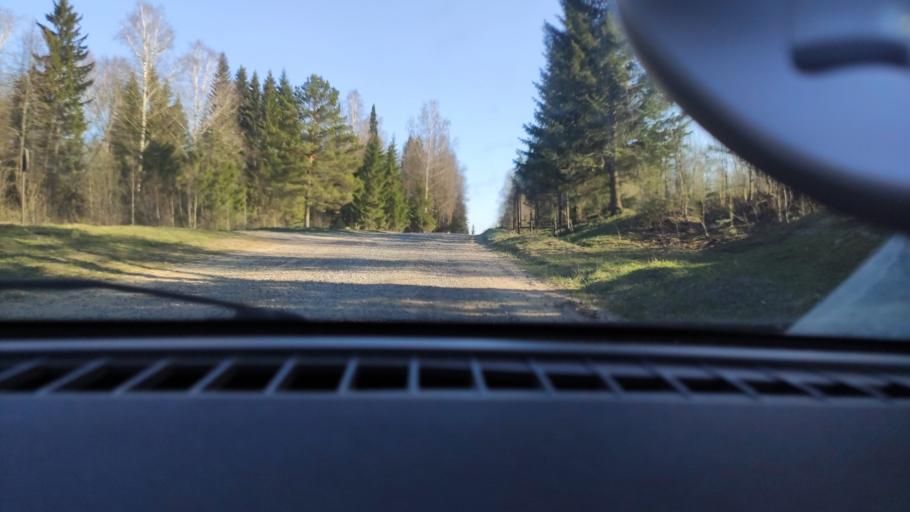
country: RU
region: Perm
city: Polazna
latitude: 58.1338
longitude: 56.4576
